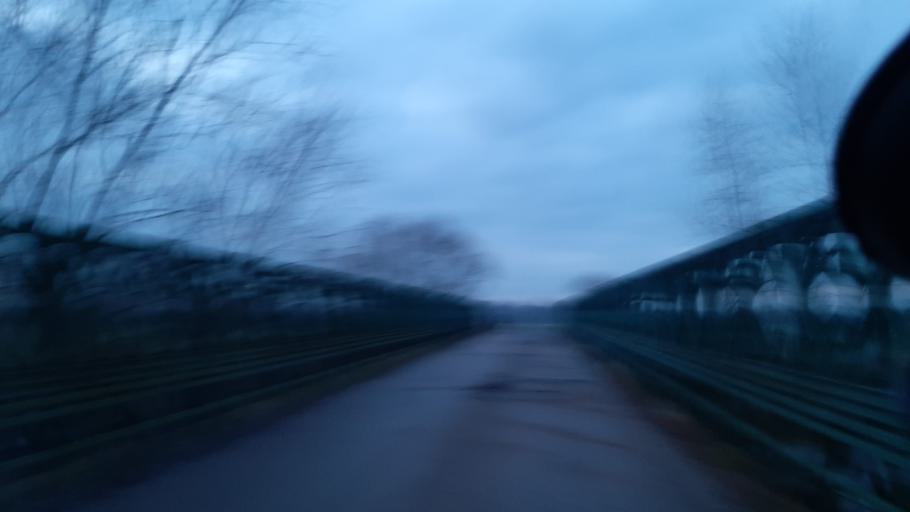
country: PL
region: Lublin Voivodeship
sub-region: Powiat lubartowski
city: Firlej
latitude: 51.5769
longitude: 22.5408
